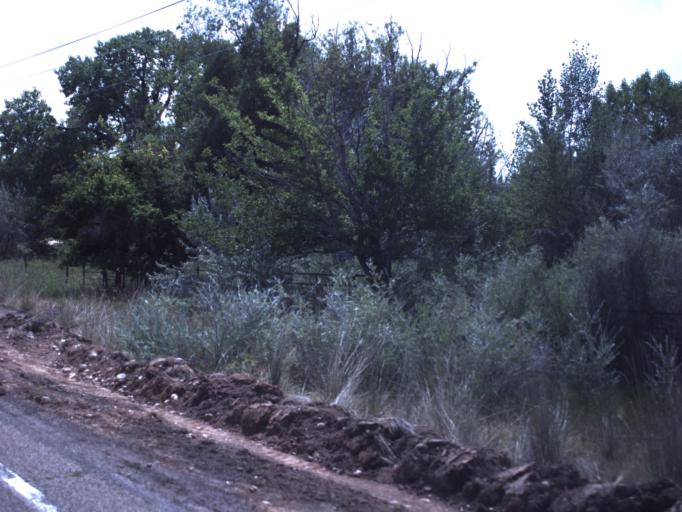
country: US
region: Utah
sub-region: Duchesne County
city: Roosevelt
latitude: 40.3742
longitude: -110.0298
